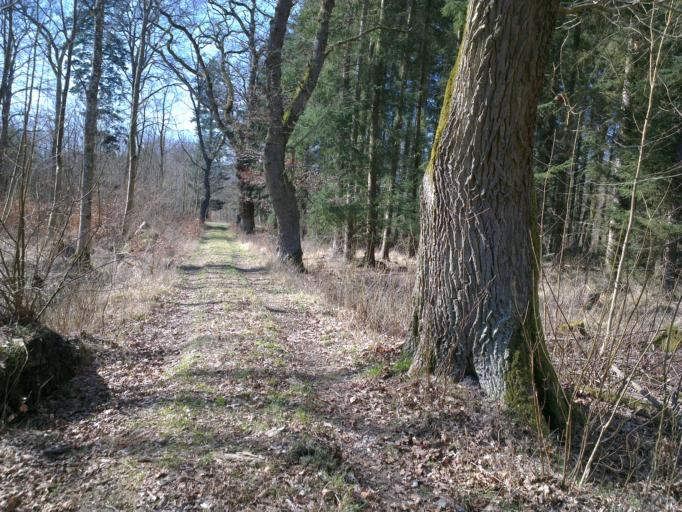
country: DK
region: Capital Region
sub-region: Frederikssund Kommune
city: Jaegerspris
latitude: 55.8812
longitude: 11.9883
